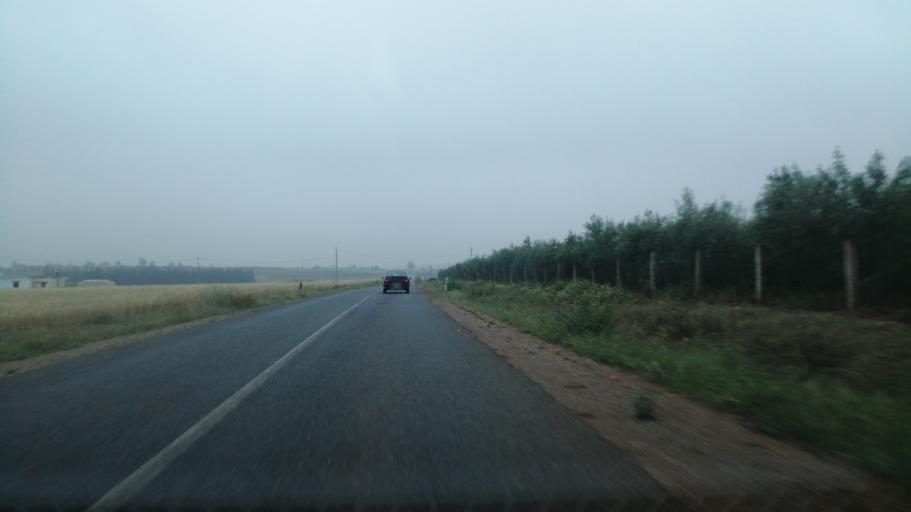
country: MA
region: Rabat-Sale-Zemmour-Zaer
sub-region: Khemisset
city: Tiflet
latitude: 33.7455
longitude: -6.2685
